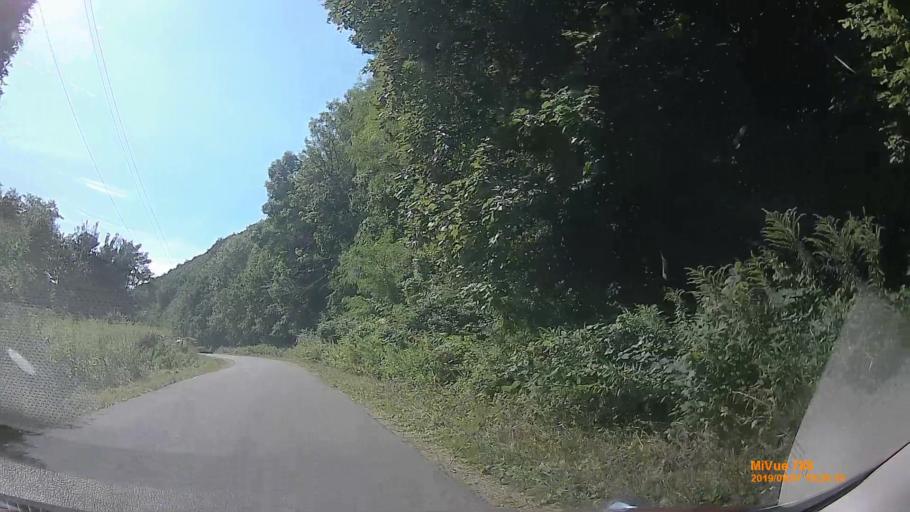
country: HU
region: Veszprem
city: Ajka
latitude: 47.0773
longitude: 17.5782
